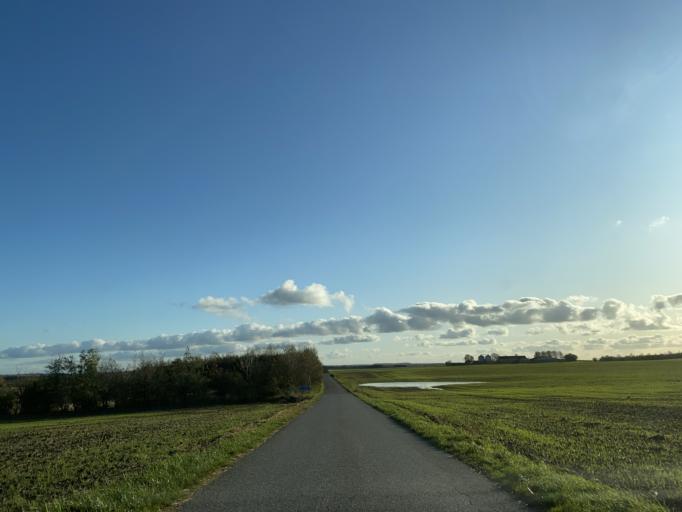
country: DK
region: Central Jutland
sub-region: Viborg Kommune
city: Bjerringbro
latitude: 56.3408
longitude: 9.7146
